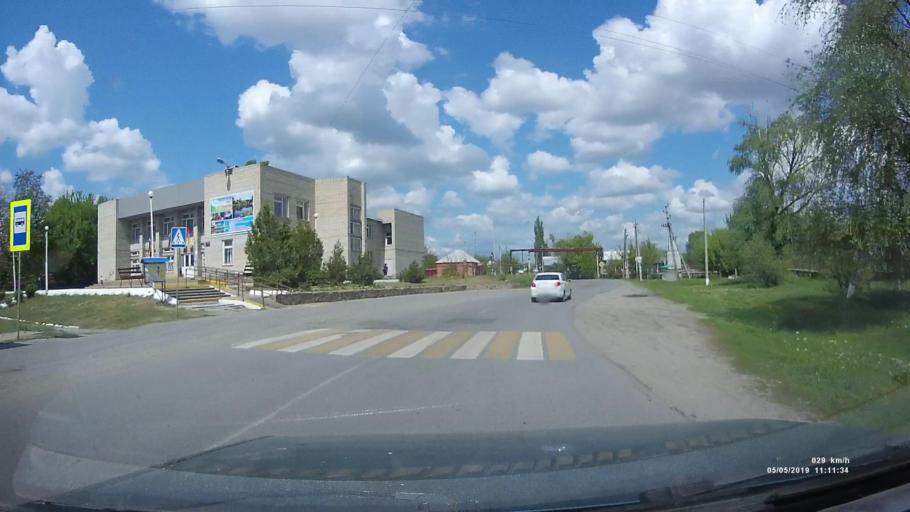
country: RU
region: Rostov
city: Ust'-Donetskiy
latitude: 47.7465
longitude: 40.9444
